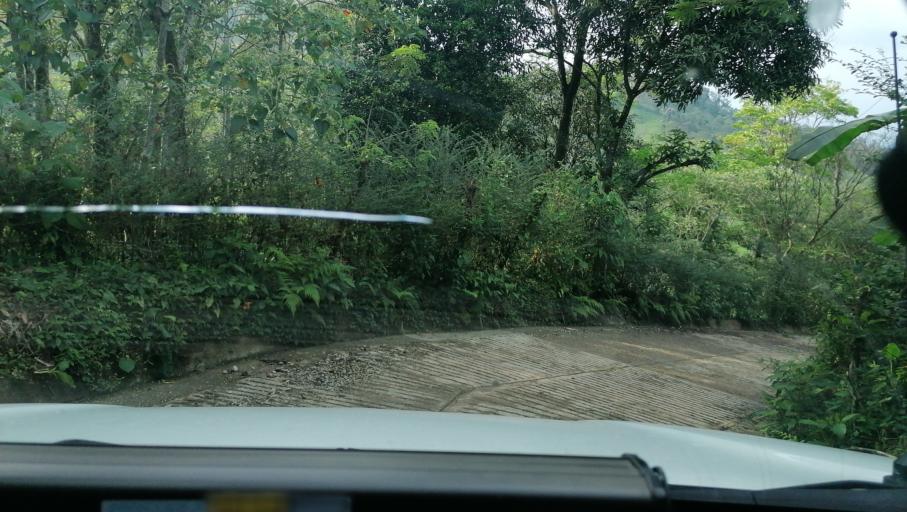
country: MX
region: Chiapas
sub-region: Tapilula
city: San Francisco Jacona
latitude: 17.3291
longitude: -93.1015
